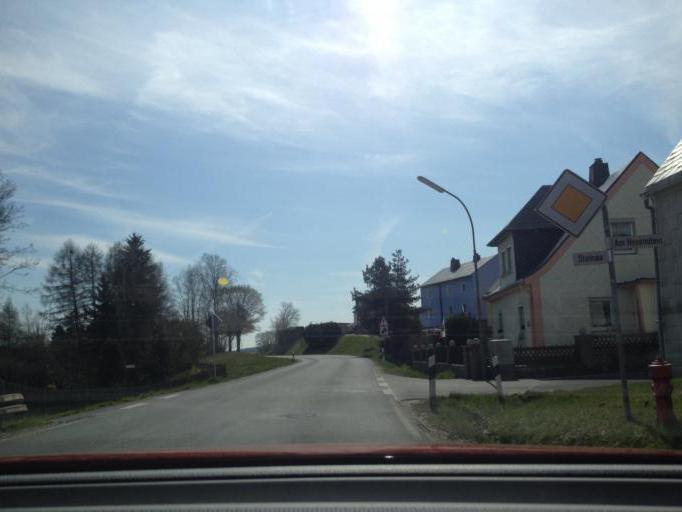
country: DE
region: Bavaria
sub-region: Upper Franconia
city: Weissenstadt
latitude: 50.0983
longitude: 11.8855
